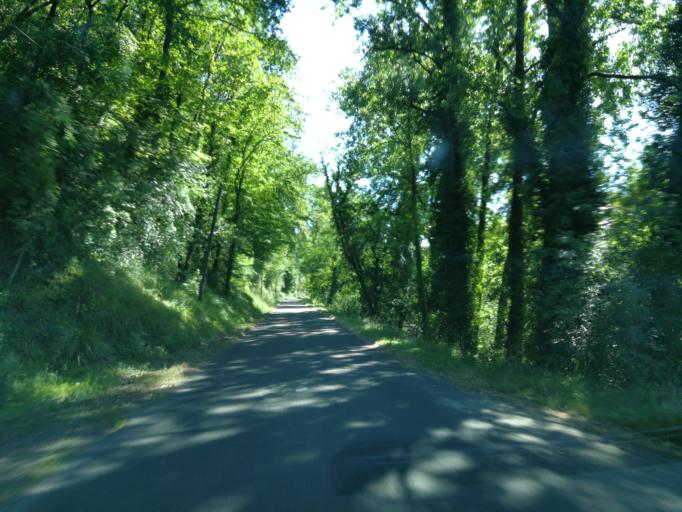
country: FR
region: Aquitaine
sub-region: Departement de la Dordogne
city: Eyvigues-et-Eybenes
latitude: 44.8710
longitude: 1.3808
